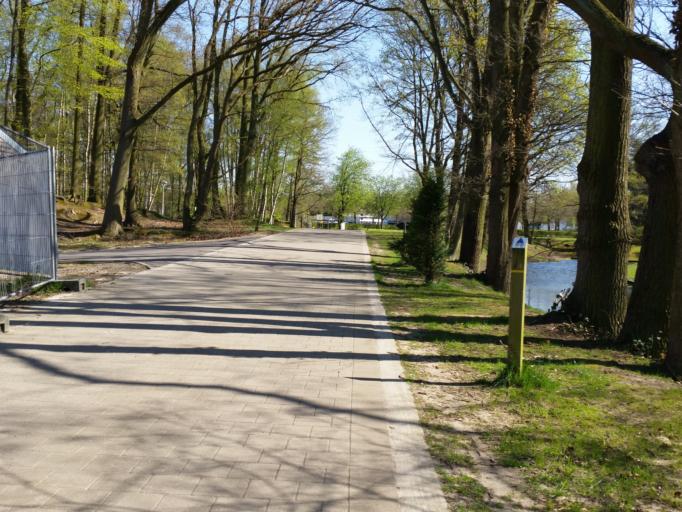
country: BE
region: Flanders
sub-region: Provincie Antwerpen
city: Bonheiden
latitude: 50.9870
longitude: 4.5174
